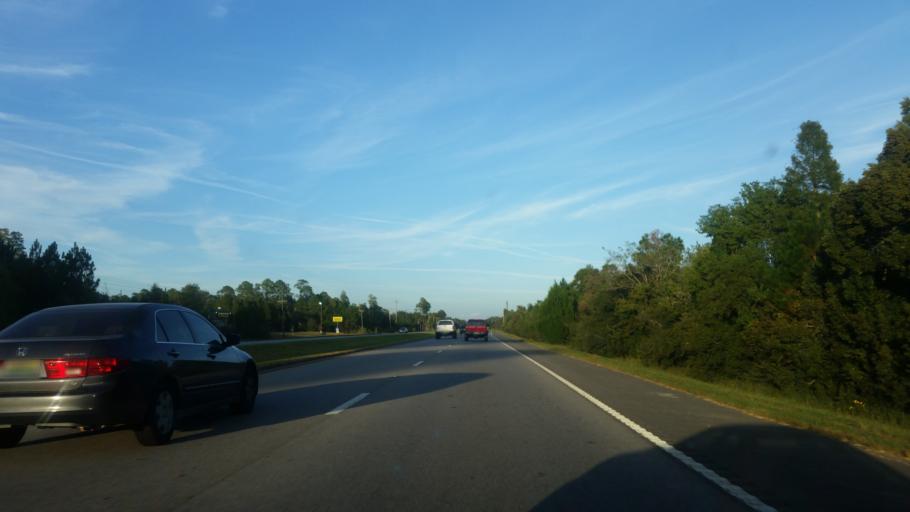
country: US
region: Mississippi
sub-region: Jackson County
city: Moss Point
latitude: 30.4156
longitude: -88.4676
